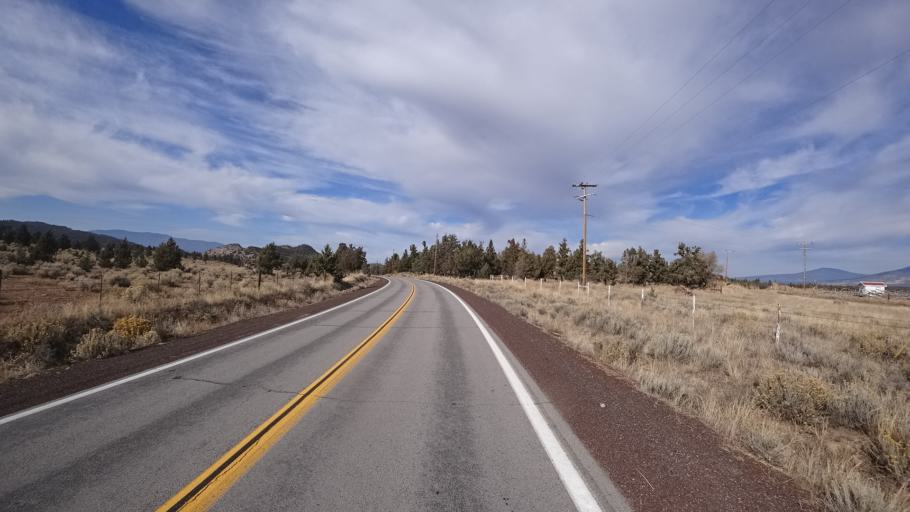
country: US
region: California
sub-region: Siskiyou County
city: Weed
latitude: 41.5524
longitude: -122.3811
